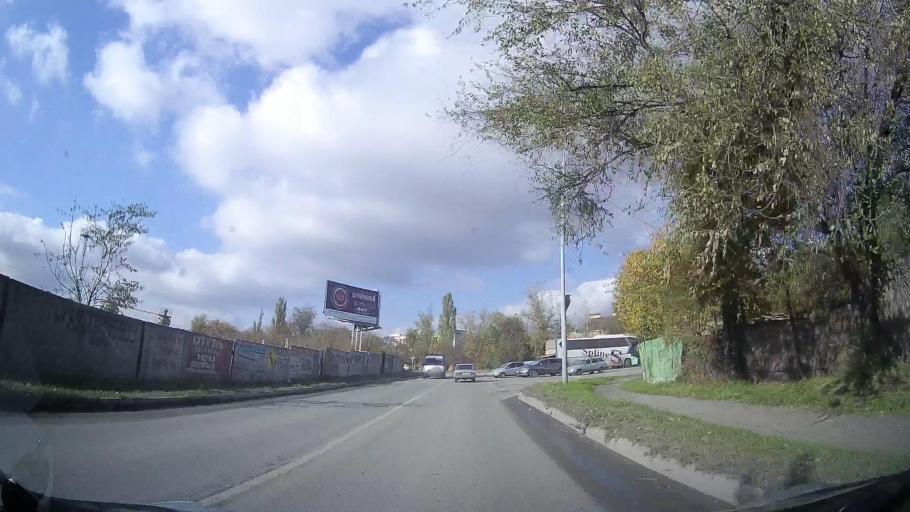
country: RU
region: Rostov
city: Rostov-na-Donu
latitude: 47.2256
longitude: 39.6826
